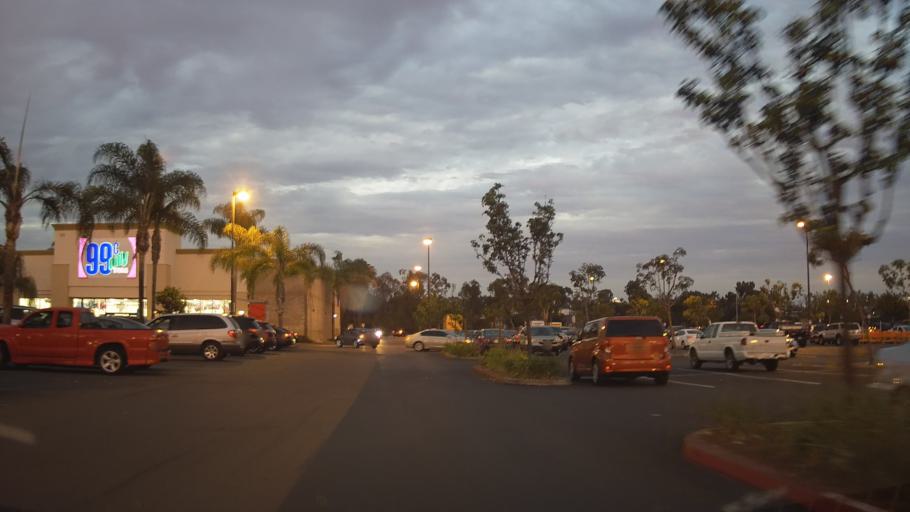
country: US
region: California
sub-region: San Diego County
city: National City
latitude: 32.7032
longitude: -117.1012
